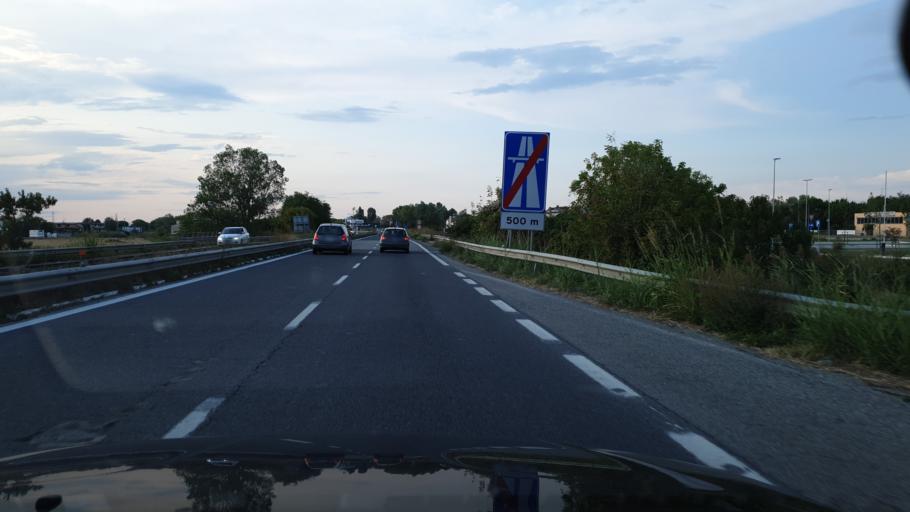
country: IT
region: Emilia-Romagna
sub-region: Forli-Cesena
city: Cesenatico
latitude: 44.1831
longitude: 12.4105
